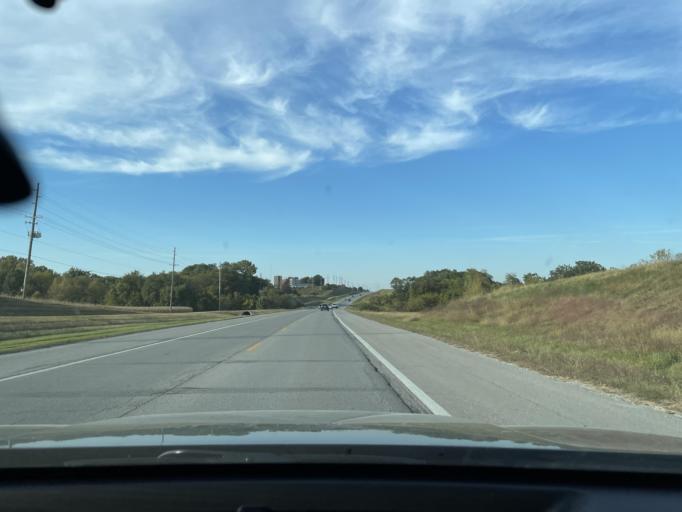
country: US
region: Missouri
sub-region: Buchanan County
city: Saint Joseph
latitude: 39.7631
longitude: -94.7687
